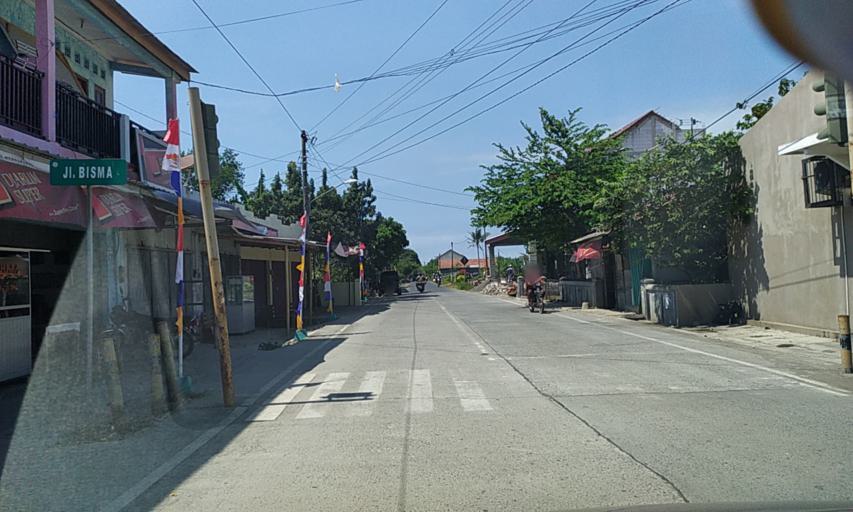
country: ID
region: Central Java
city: Rejanegara
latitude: -7.6865
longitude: 109.0476
